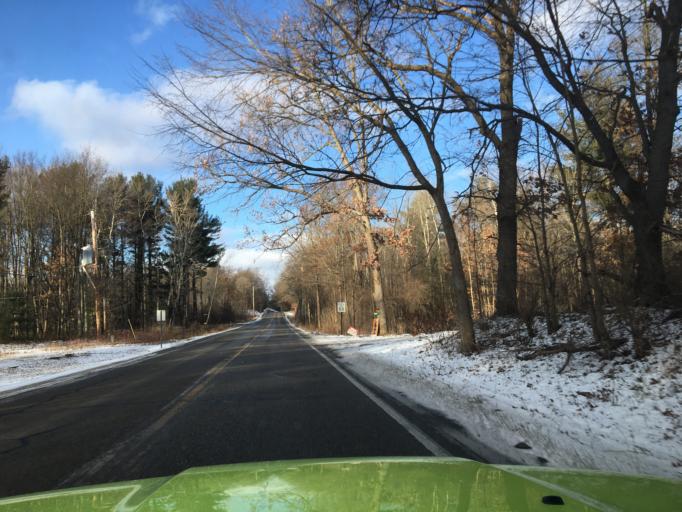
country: US
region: Michigan
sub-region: Montcalm County
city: Greenville
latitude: 43.1919
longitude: -85.2829
